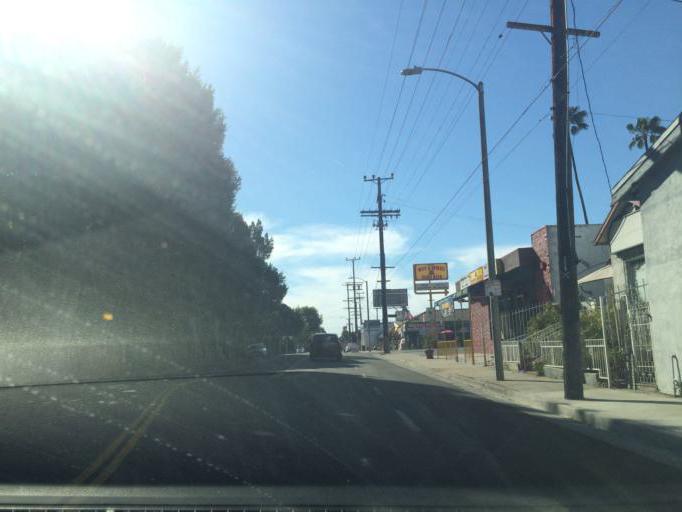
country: US
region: California
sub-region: Los Angeles County
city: Hollywood
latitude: 34.0835
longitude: -118.3312
